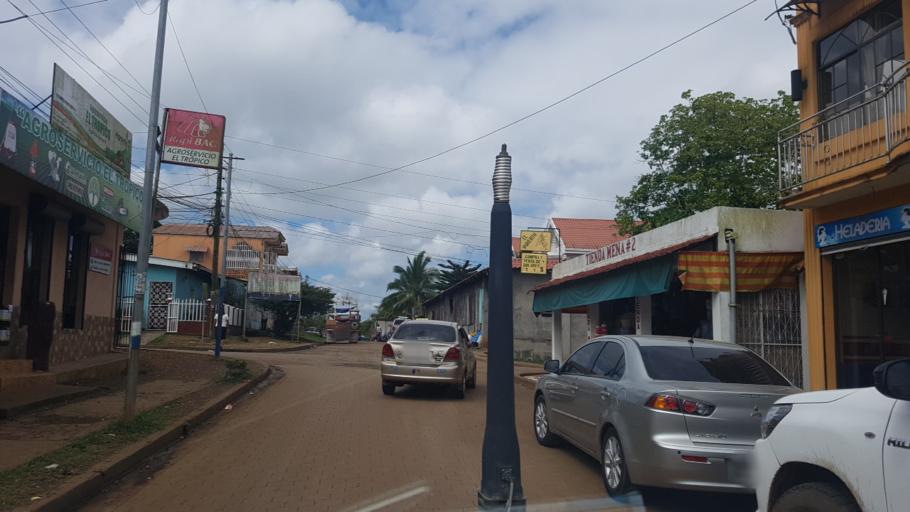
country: NI
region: Atlantico Sur
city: Nueva Guinea
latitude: 11.6903
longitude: -84.4528
